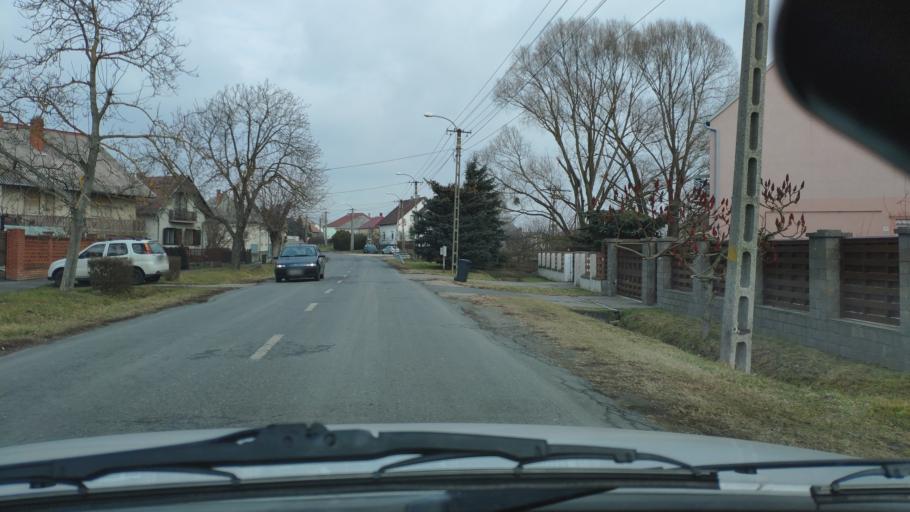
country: HU
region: Zala
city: Nagykanizsa
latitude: 46.4527
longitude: 16.9485
